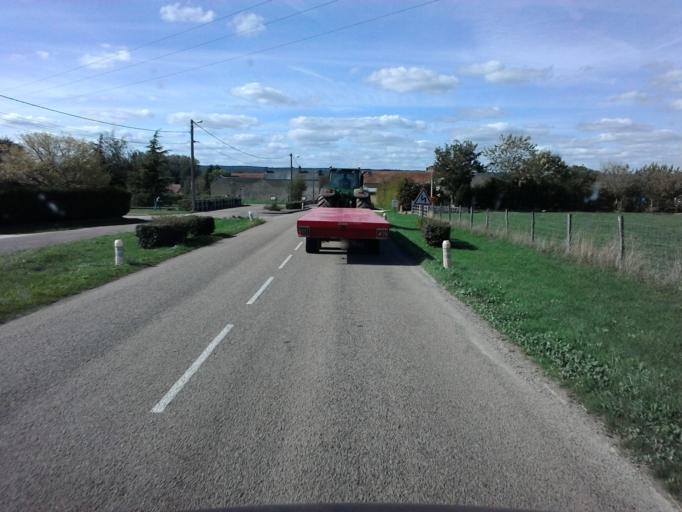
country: FR
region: Bourgogne
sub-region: Departement de la Cote-d'Or
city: Chatillon-sur-Seine
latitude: 47.9143
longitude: 4.6700
